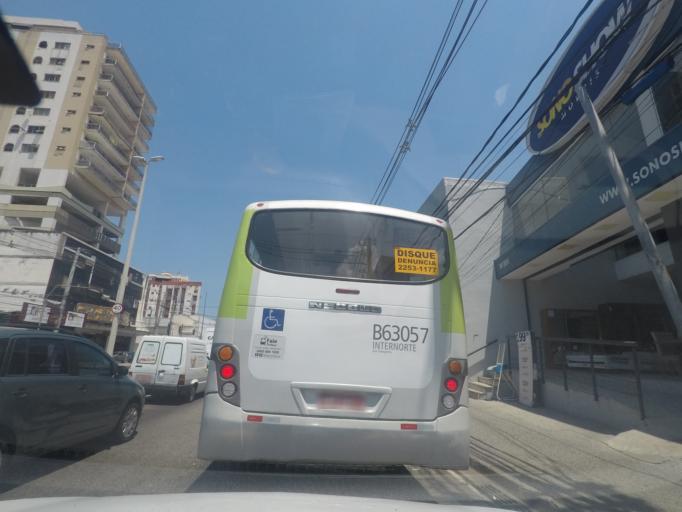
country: BR
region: Rio de Janeiro
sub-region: Duque De Caxias
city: Duque de Caxias
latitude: -22.8397
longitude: -43.2825
